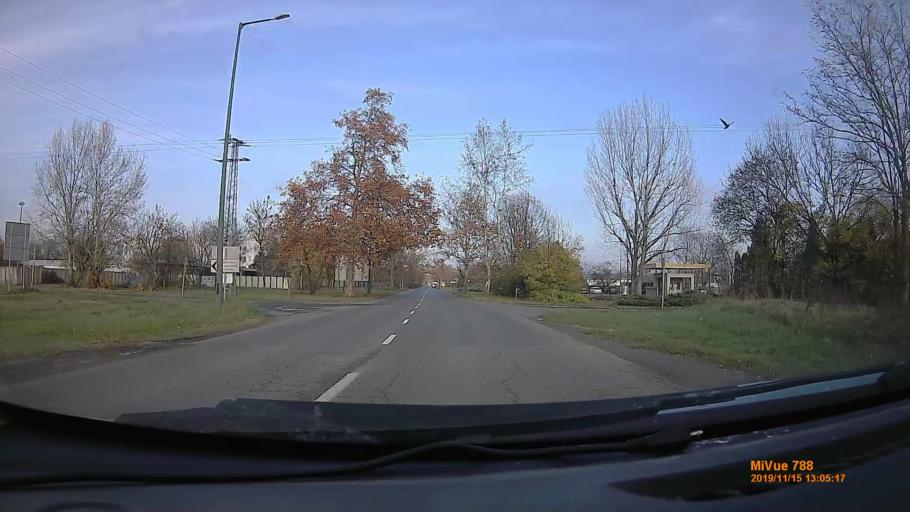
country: HU
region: Bekes
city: Gyula
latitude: 46.6353
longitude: 21.2596
